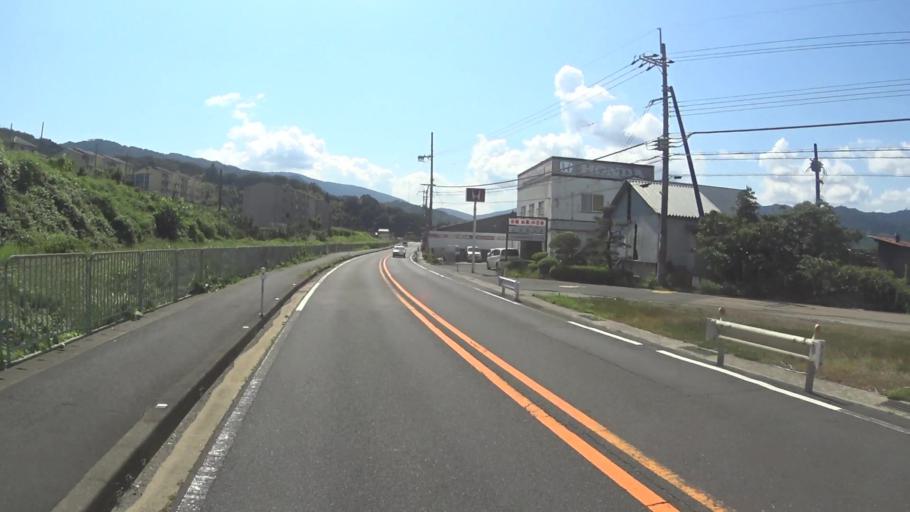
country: JP
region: Kyoto
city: Miyazu
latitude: 35.5444
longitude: 135.2104
